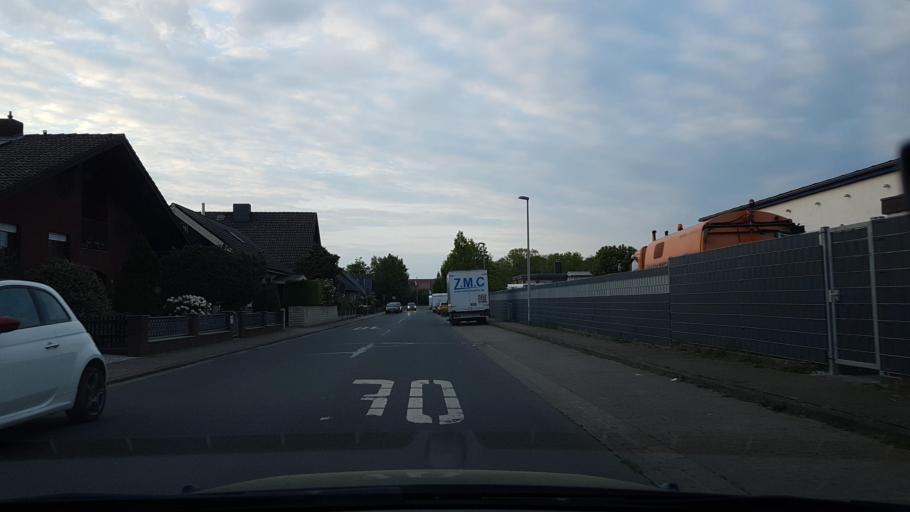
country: DE
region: Lower Saxony
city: Garbsen
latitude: 52.4391
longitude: 9.5503
